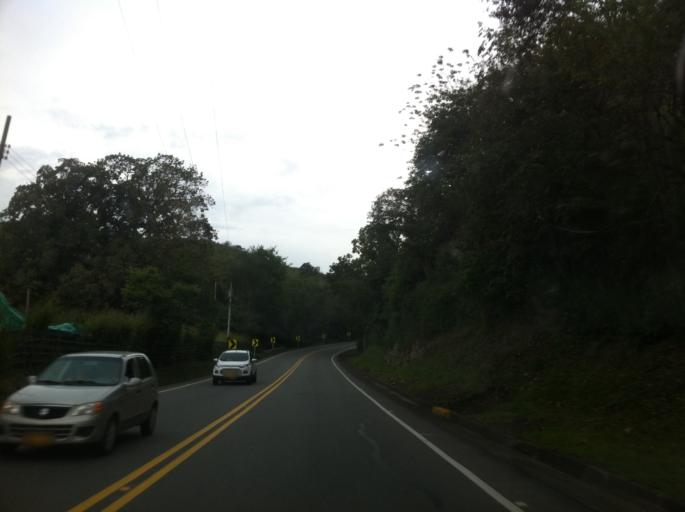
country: CO
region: Valle del Cauca
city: Zarzal
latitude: 4.3513
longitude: -76.0358
